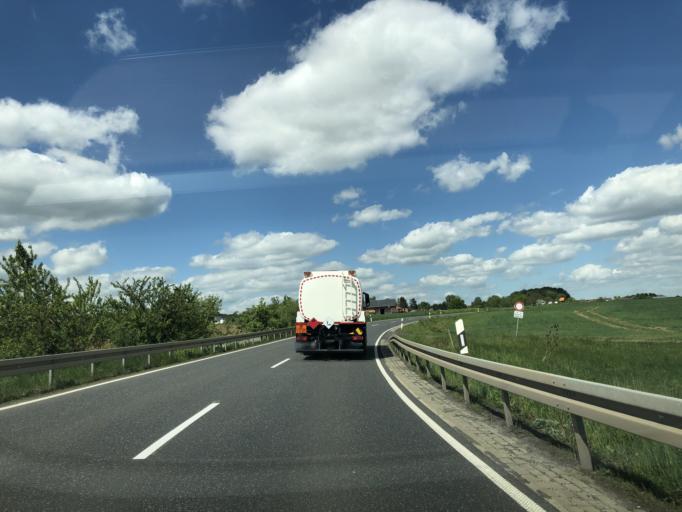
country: DE
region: Hesse
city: Gudensberg
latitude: 51.1864
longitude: 9.4091
